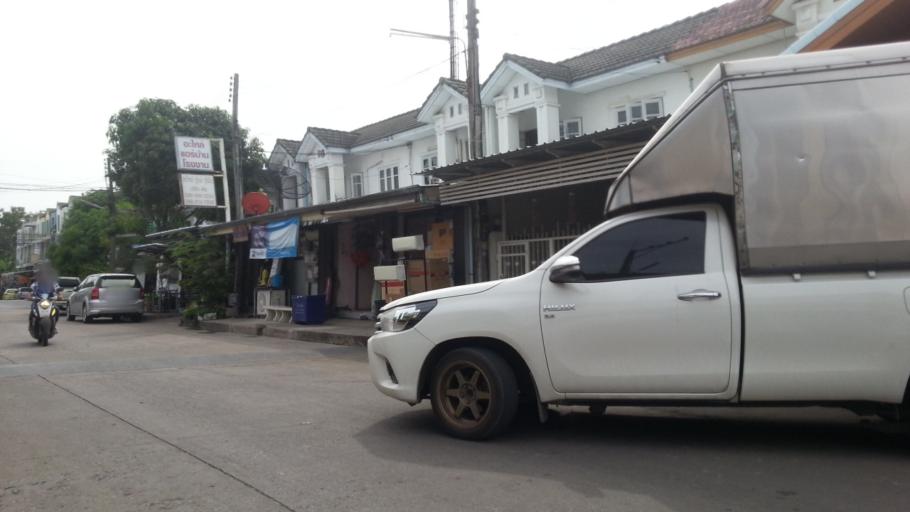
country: TH
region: Pathum Thani
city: Ban Rangsit
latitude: 14.0412
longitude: 100.7951
